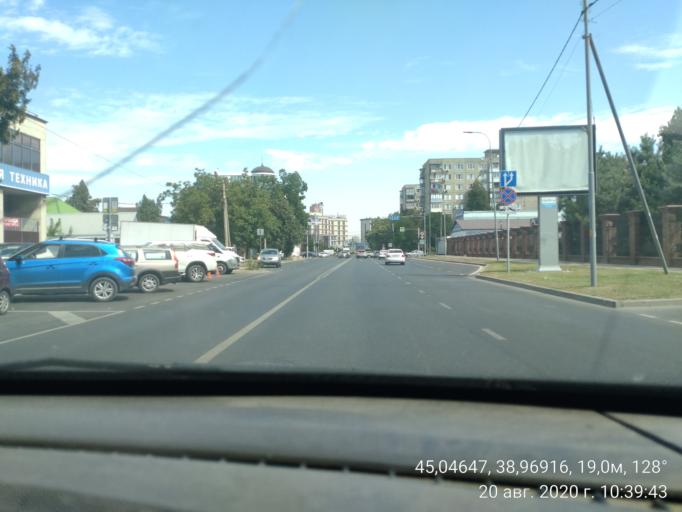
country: RU
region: Krasnodarskiy
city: Krasnodar
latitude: 45.0465
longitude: 38.9691
